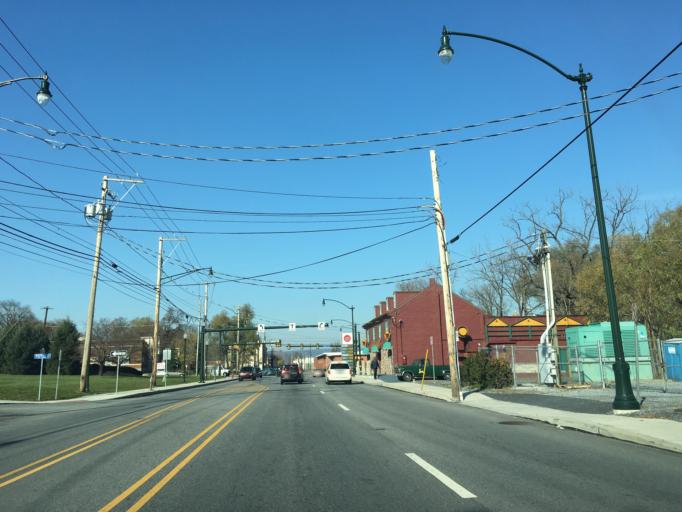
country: US
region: Pennsylvania
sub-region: Dauphin County
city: Harrisburg
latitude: 40.2800
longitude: -76.8880
